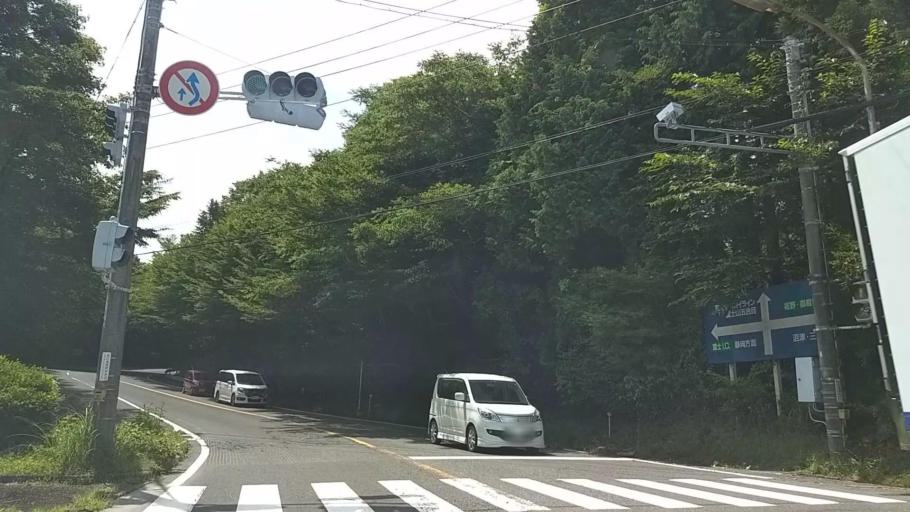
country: JP
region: Shizuoka
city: Gotemba
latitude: 35.2603
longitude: 138.8140
